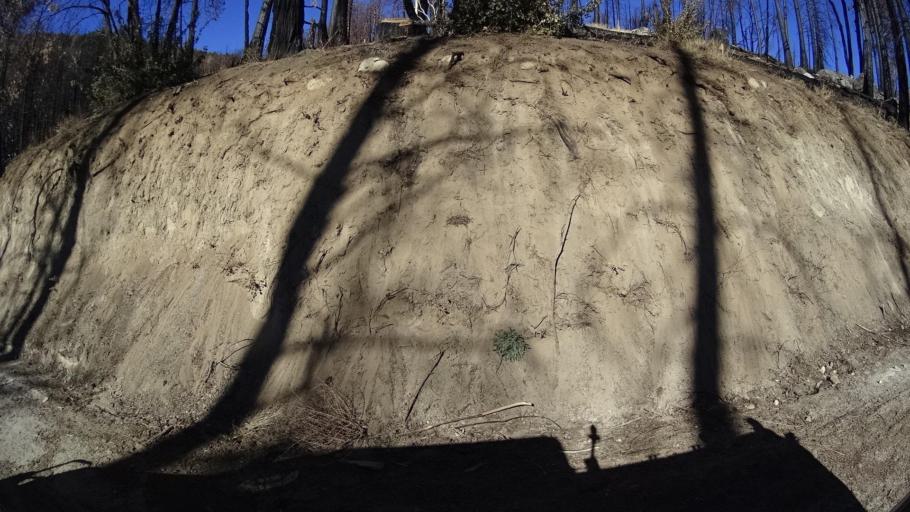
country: US
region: California
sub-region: Kern County
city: Alta Sierra
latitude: 35.7187
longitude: -118.5443
